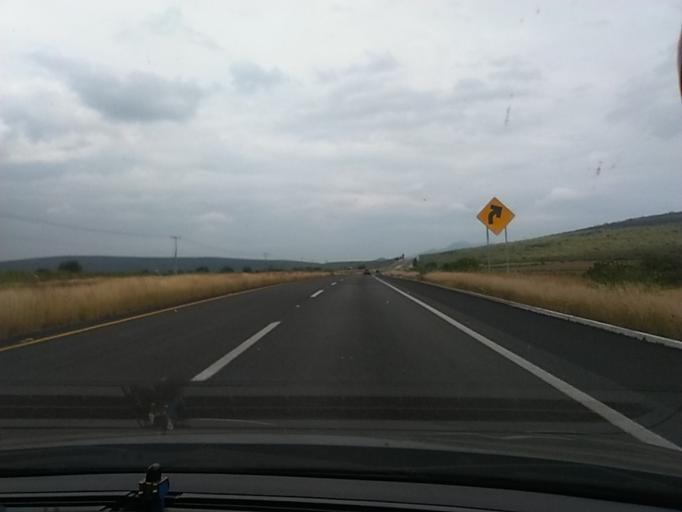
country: MX
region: Michoacan
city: Ecuandureo
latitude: 20.1738
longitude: -102.1654
